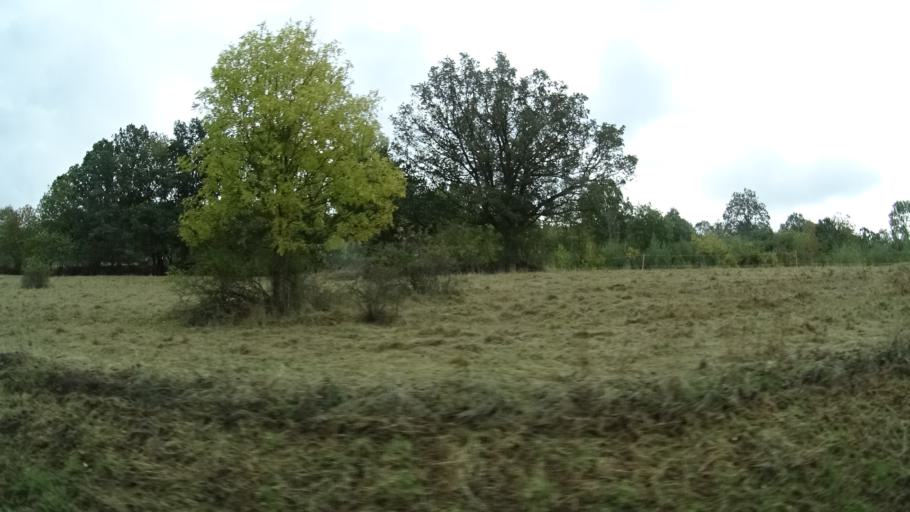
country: DE
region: Thuringia
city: Unterkatz
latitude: 50.6230
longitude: 10.2660
